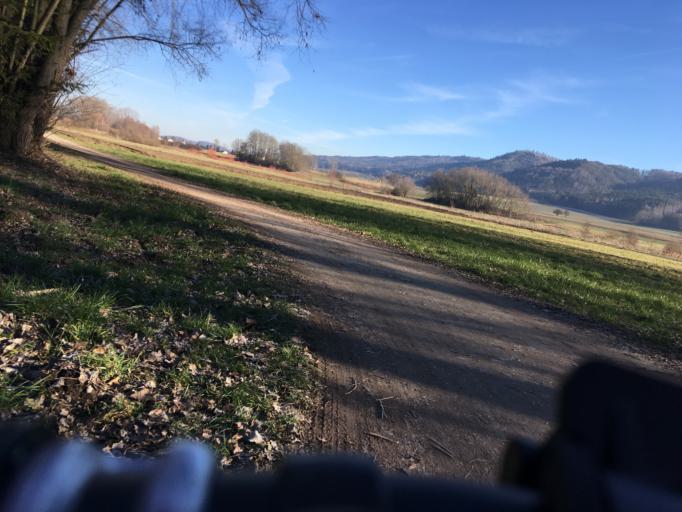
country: DE
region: Baden-Wuerttemberg
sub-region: Freiburg Region
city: Rielasingen-Worblingen
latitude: 47.7213
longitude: 8.8720
